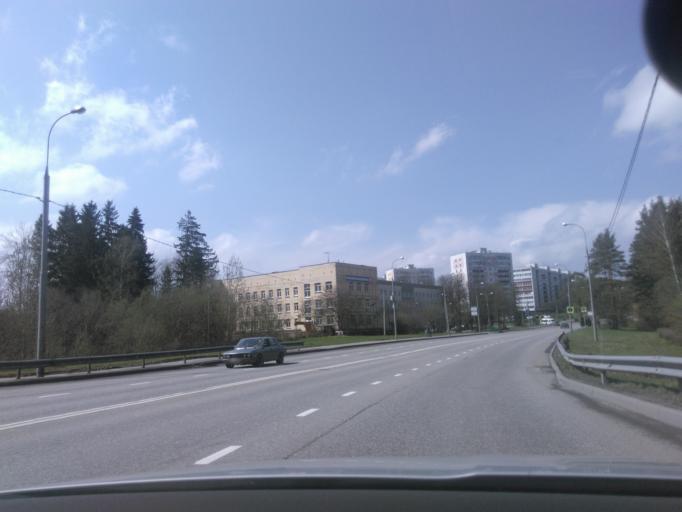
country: RU
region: Moskovskaya
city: Rzhavki
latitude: 55.9843
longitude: 37.2408
